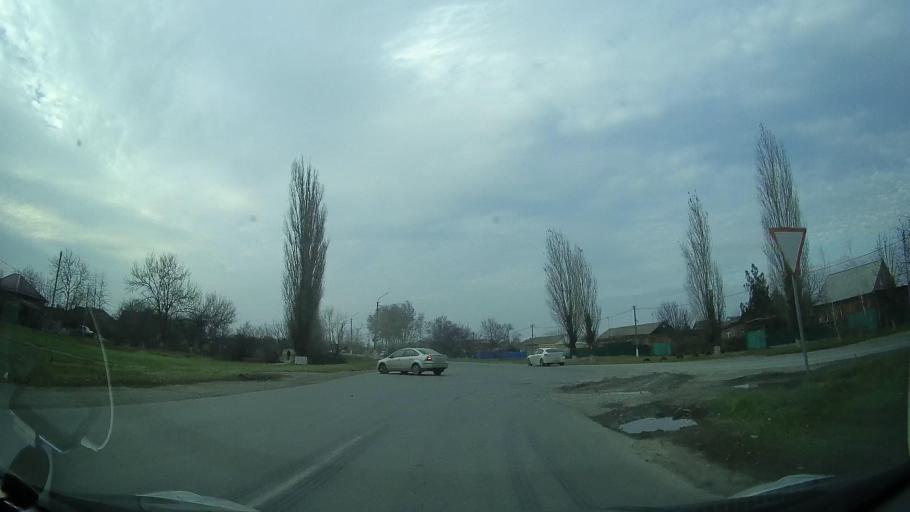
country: RU
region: Rostov
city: Ol'ginskaya
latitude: 47.1825
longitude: 39.9581
